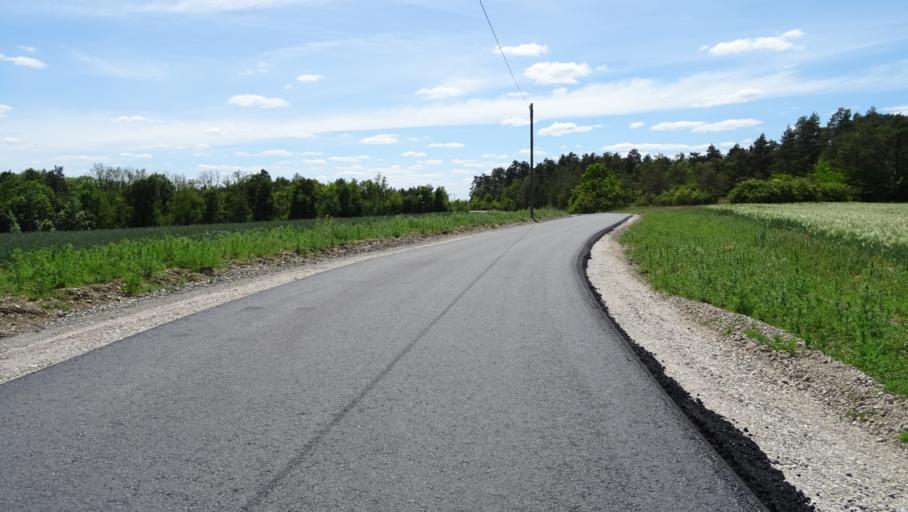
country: DE
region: Baden-Wuerttemberg
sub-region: Karlsruhe Region
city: Seckach
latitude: 49.4817
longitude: 9.3280
